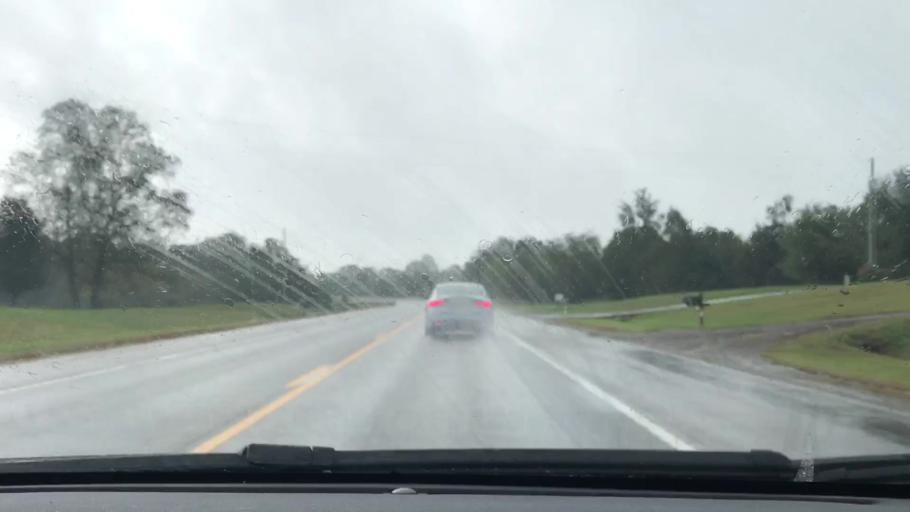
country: US
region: Tennessee
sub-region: Macon County
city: Lafayette
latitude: 36.5188
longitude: -86.1303
